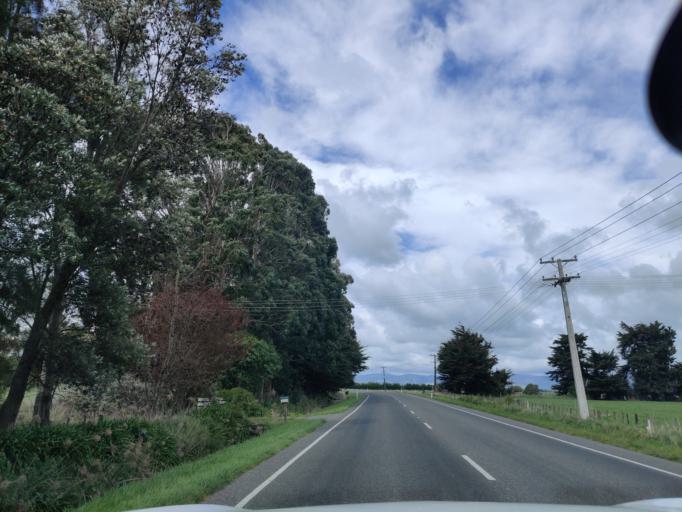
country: NZ
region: Manawatu-Wanganui
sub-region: Palmerston North City
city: Palmerston North
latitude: -40.3270
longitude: 175.5066
